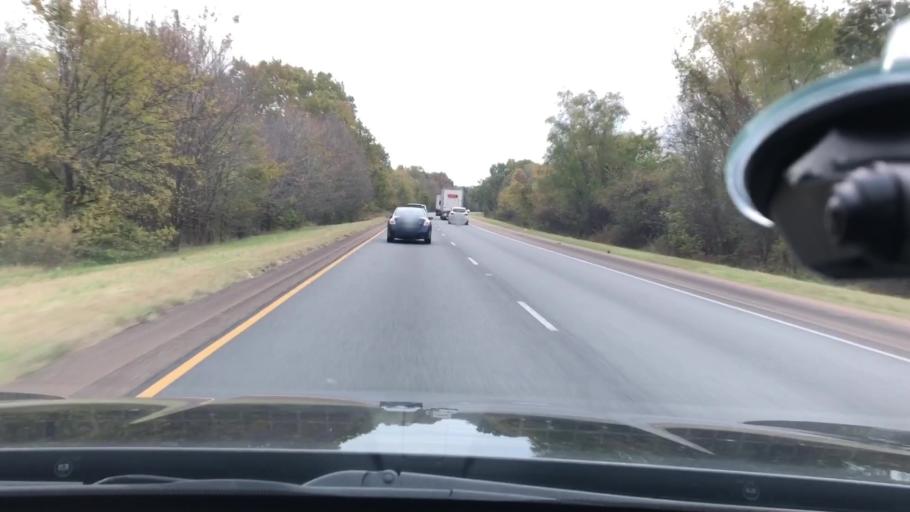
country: US
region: Arkansas
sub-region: Nevada County
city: Prescott
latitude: 33.8431
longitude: -93.3803
